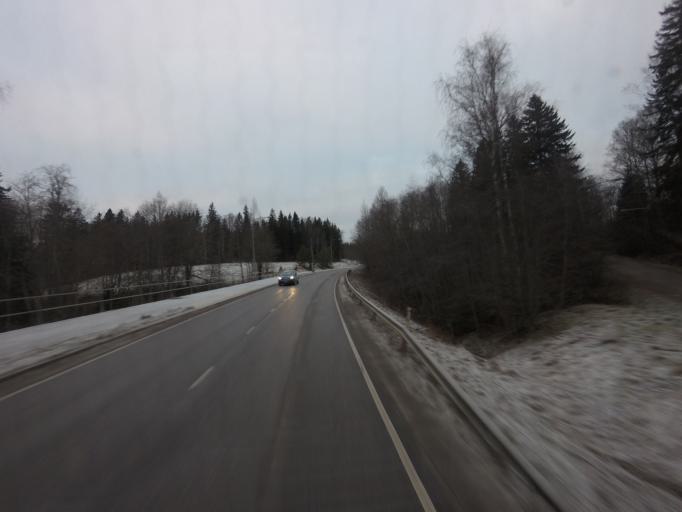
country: FI
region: Uusimaa
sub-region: Helsinki
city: Espoo
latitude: 60.2209
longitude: 24.6208
